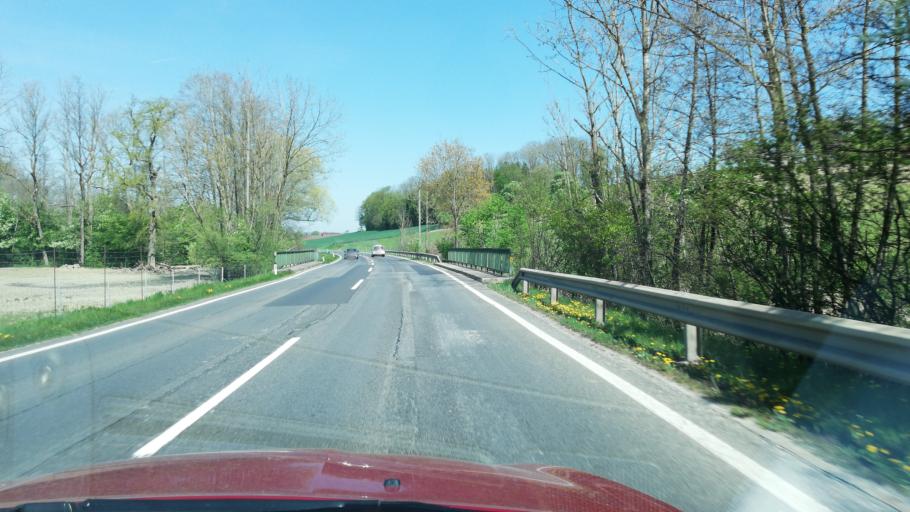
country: AT
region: Upper Austria
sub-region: Wels-Land
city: Thalheim bei Wels
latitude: 48.1299
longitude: 14.0519
